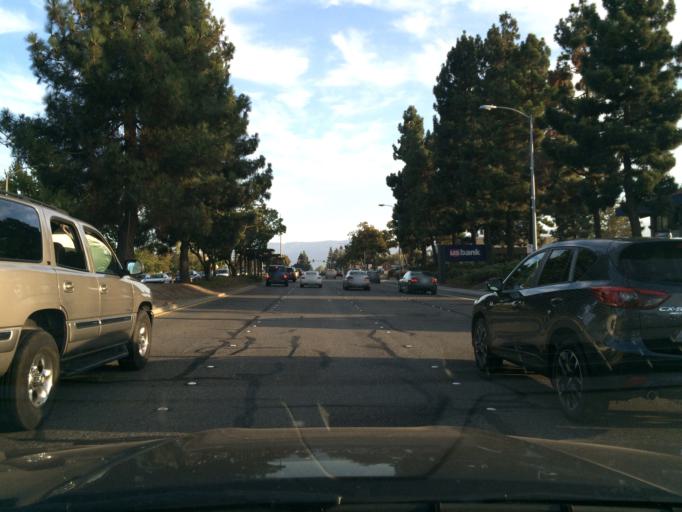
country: US
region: California
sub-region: Santa Clara County
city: Cupertino
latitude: 37.3184
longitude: -122.0324
